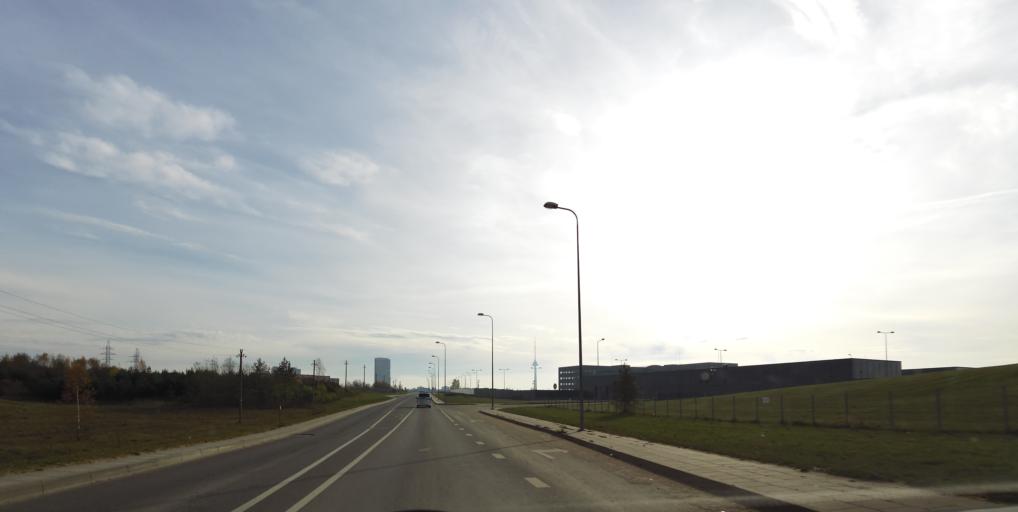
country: LT
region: Vilnius County
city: Justiniskes
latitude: 54.7102
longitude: 25.2013
